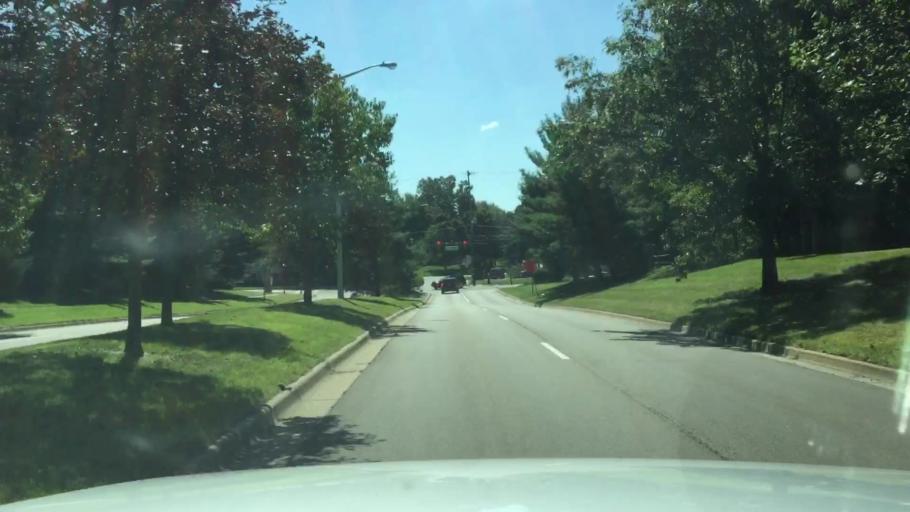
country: US
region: Michigan
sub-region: Kalamazoo County
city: Portage
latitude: 42.2167
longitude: -85.6032
